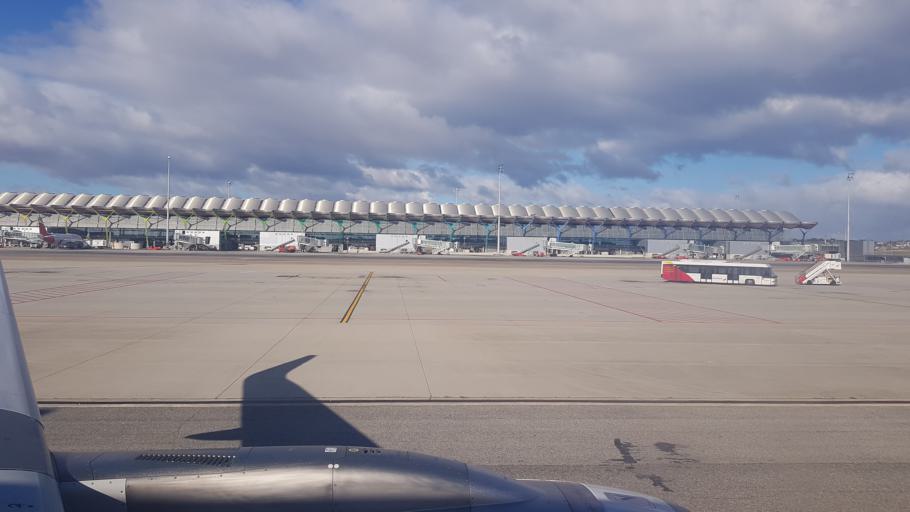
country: ES
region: Madrid
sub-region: Provincia de Madrid
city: Barajas de Madrid
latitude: 40.4946
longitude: -3.5864
